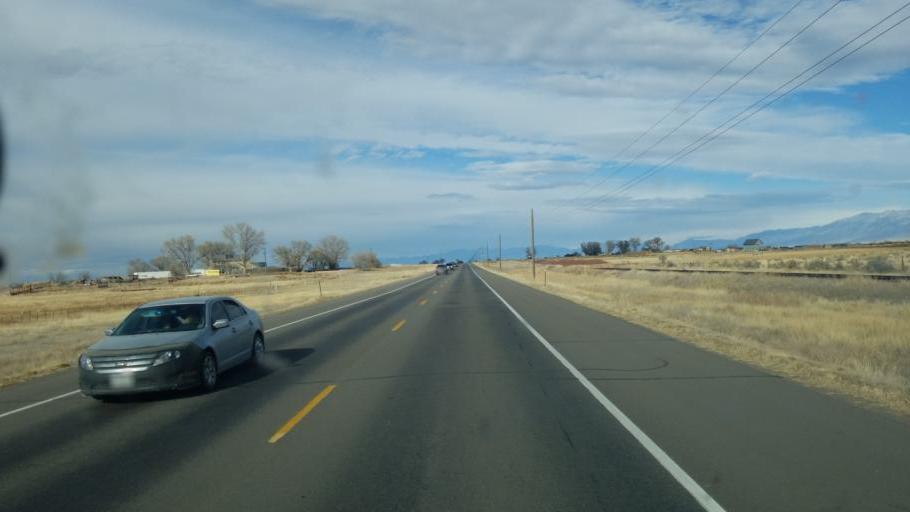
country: US
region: Colorado
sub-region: Alamosa County
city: Alamosa
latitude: 37.3429
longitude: -105.9367
